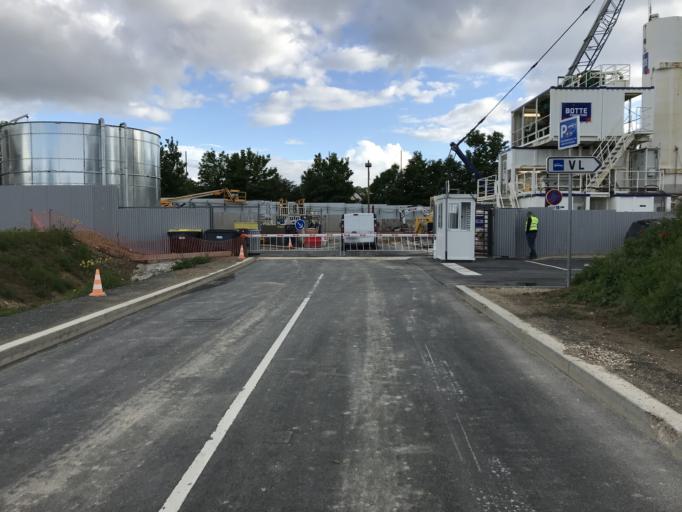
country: FR
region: Ile-de-France
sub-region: Departement de l'Essonne
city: Wissous
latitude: 48.7350
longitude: 2.3323
